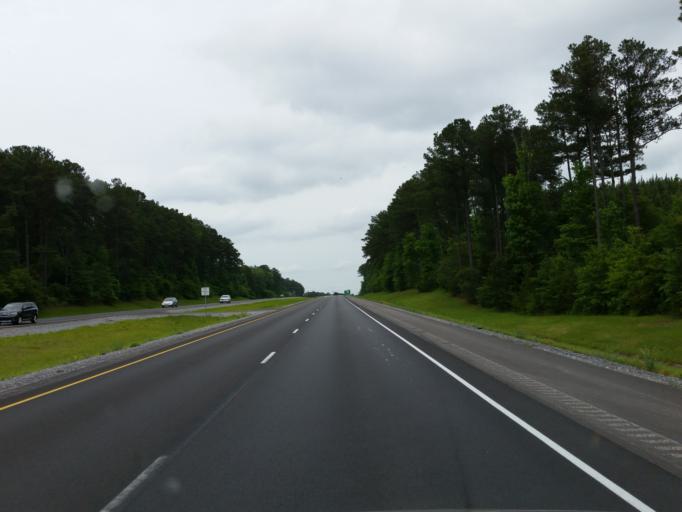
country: US
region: Mississippi
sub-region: Jones County
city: Sharon
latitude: 31.8923
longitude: -89.0325
